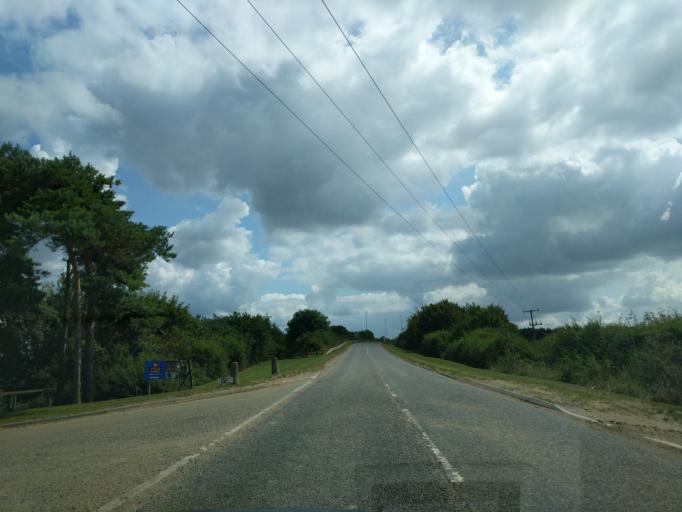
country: GB
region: England
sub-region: Cambridgeshire
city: Isleham
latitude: 52.2901
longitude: 0.4663
